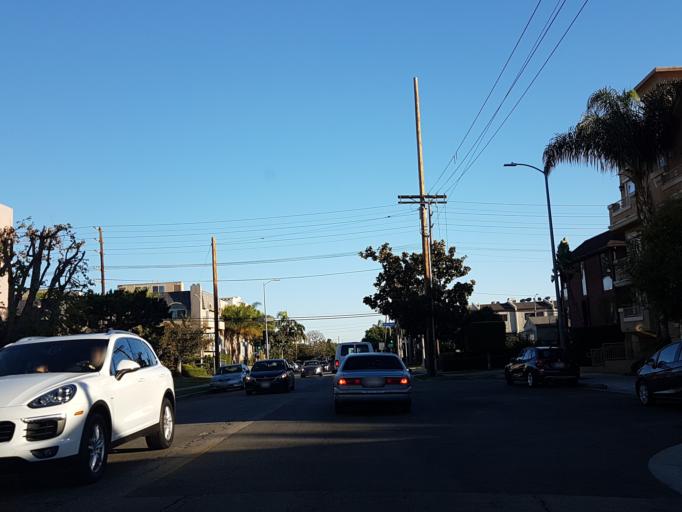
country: US
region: California
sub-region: Los Angeles County
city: Westwood, Los Angeles
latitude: 34.0406
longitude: -118.4533
